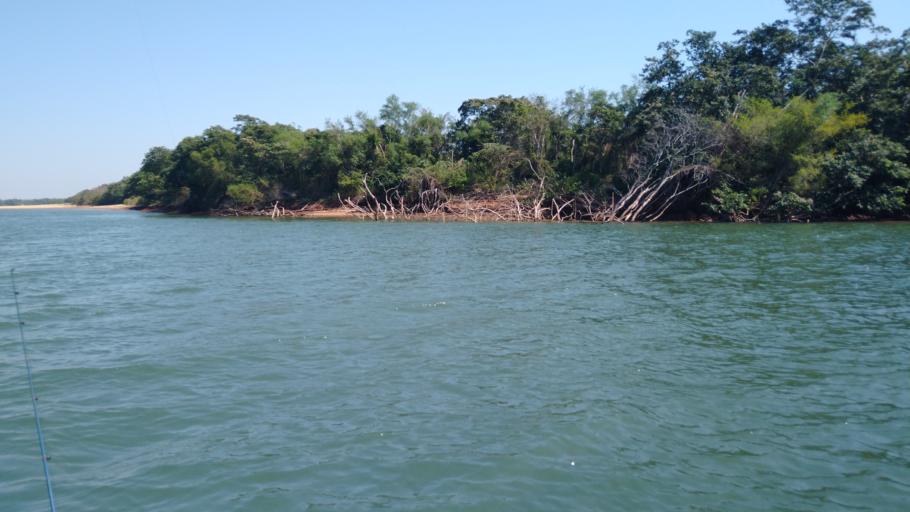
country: PY
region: Neembucu
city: Cerrito
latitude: -27.3607
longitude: -57.6745
